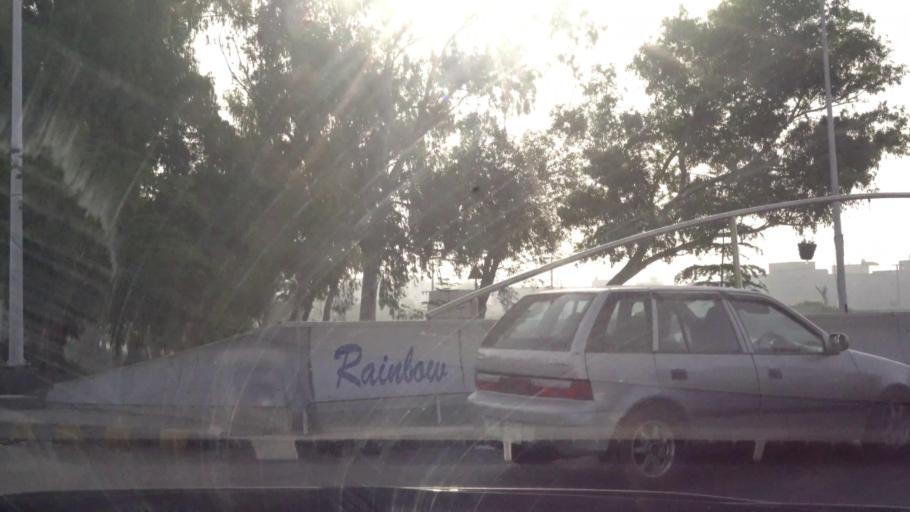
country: PK
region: Punjab
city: Faisalabad
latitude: 31.4605
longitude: 73.1741
